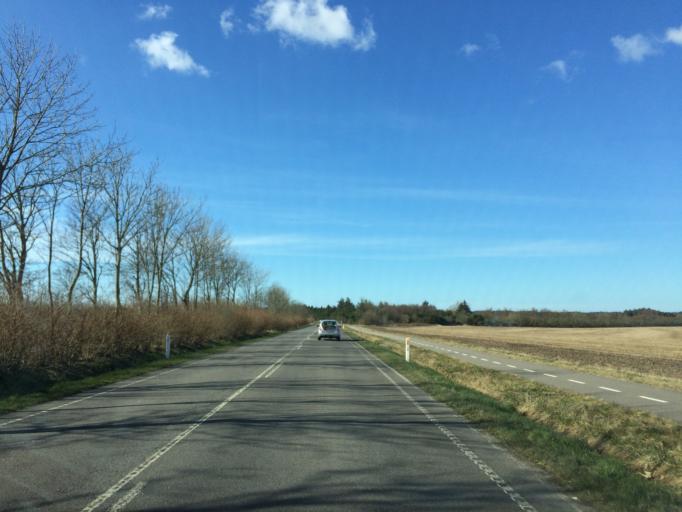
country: DK
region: South Denmark
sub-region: Varde Kommune
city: Oksbol
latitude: 55.7213
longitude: 8.2892
